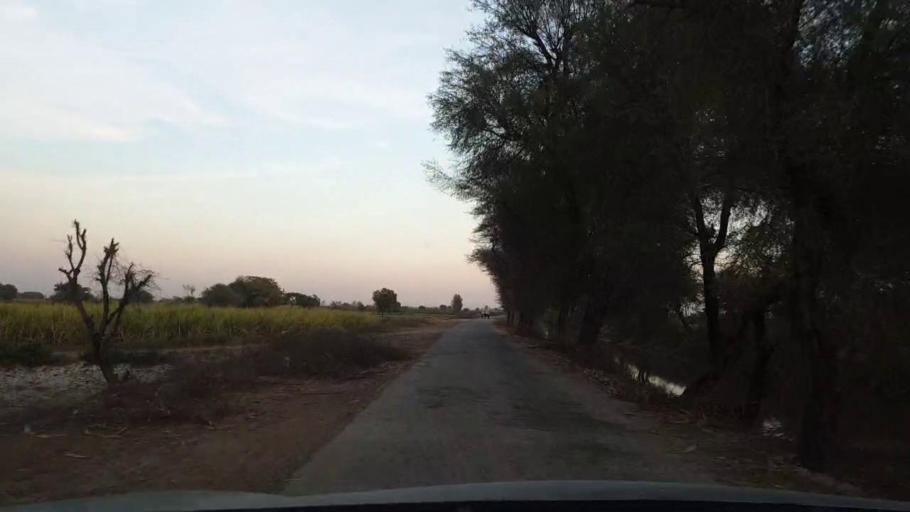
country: PK
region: Sindh
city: Tando Allahyar
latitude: 25.5969
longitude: 68.7017
